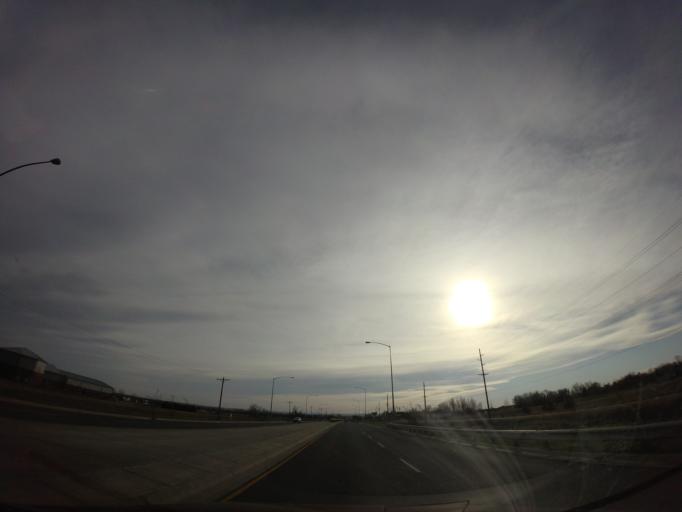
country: US
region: Montana
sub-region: Yellowstone County
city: Billings
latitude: 45.7727
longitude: -108.6176
